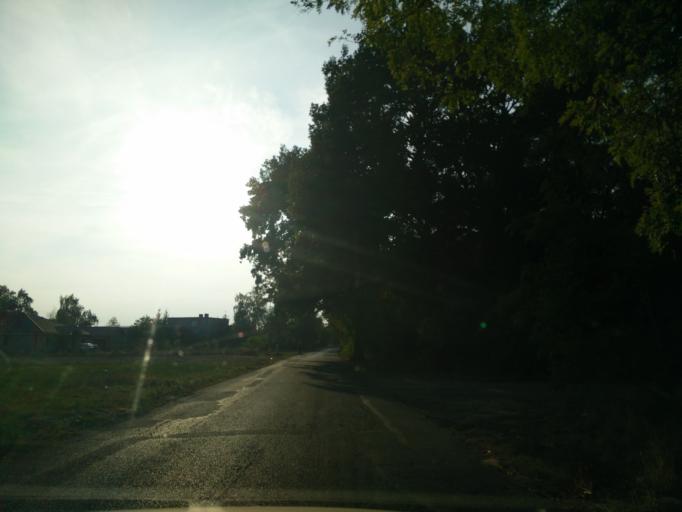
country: PL
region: Greater Poland Voivodeship
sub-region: Powiat sredzki
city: Sroda Wielkopolska
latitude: 52.1881
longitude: 17.2956
